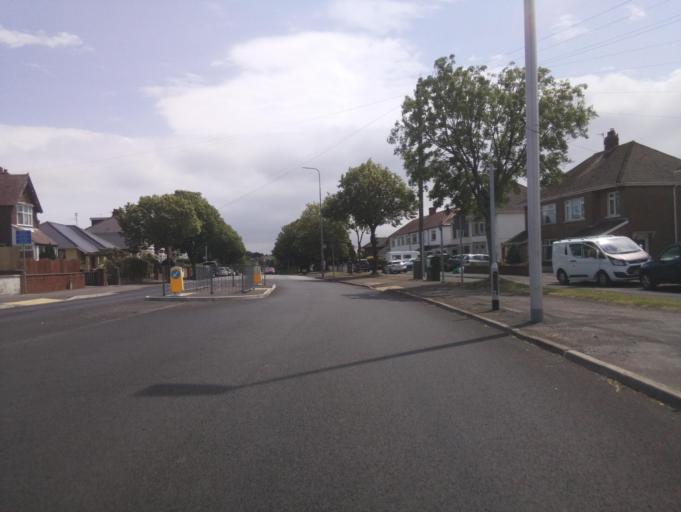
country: GB
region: Wales
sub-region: Vale of Glamorgan
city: Barry
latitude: 51.4086
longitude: -3.2997
